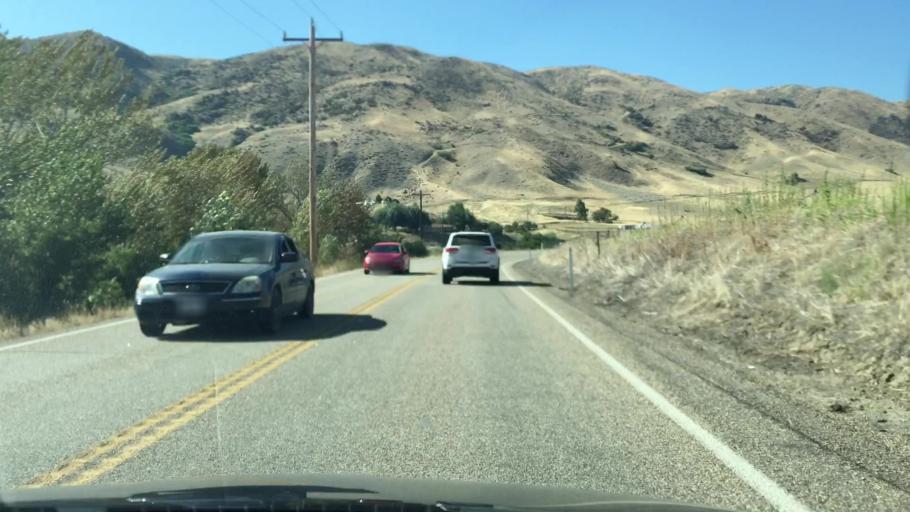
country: US
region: Idaho
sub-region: Gem County
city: Emmett
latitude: 43.9785
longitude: -116.1935
